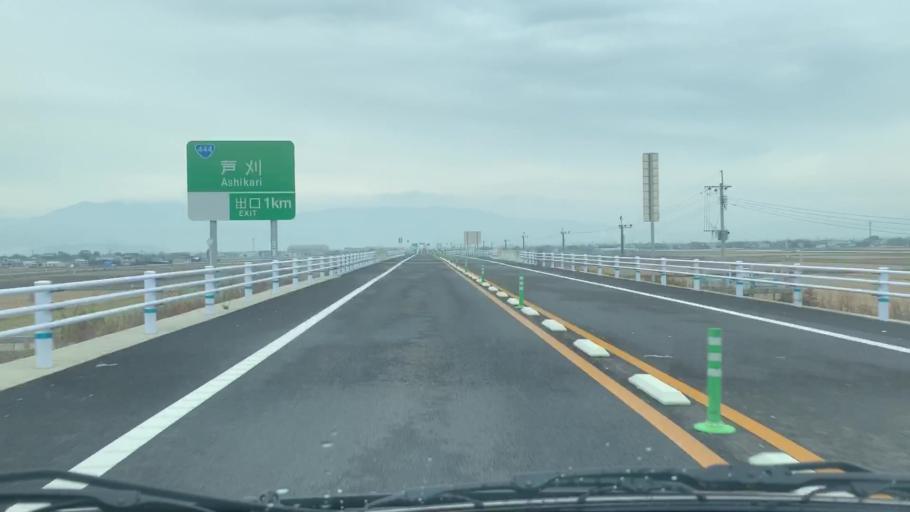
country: JP
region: Saga Prefecture
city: Saga-shi
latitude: 33.2093
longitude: 130.2149
